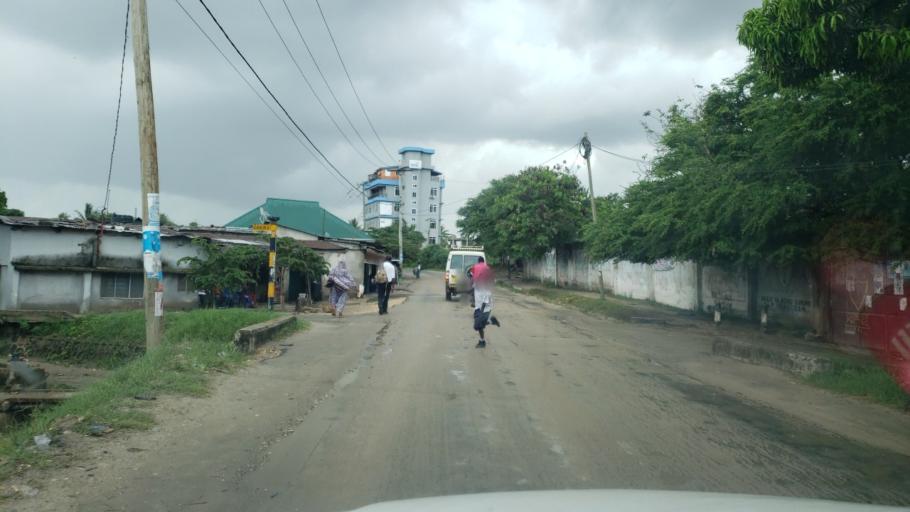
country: TZ
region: Dar es Salaam
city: Magomeni
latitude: -6.8064
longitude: 39.2505
